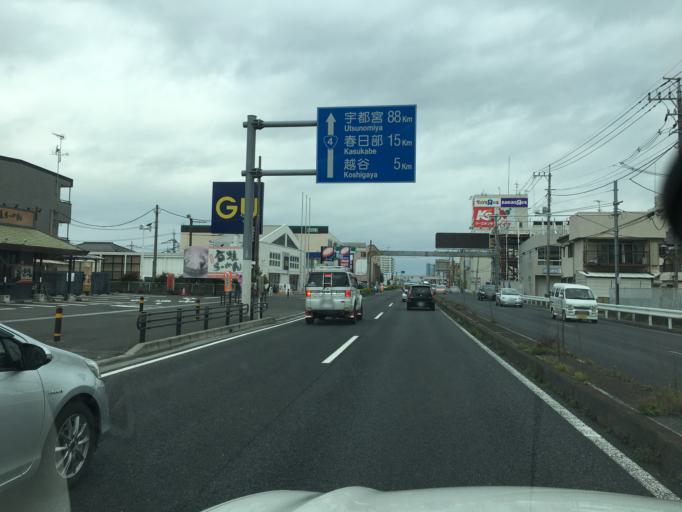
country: JP
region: Saitama
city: Koshigaya
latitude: 35.8521
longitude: 139.7844
